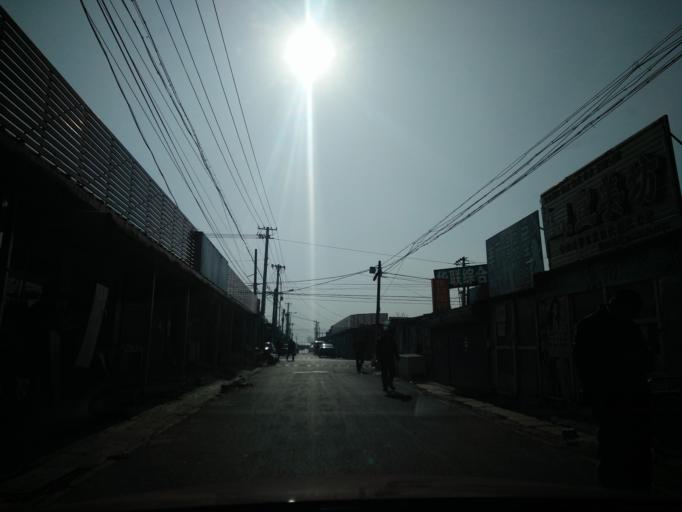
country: CN
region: Beijing
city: Yinghai
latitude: 39.7022
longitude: 116.4352
